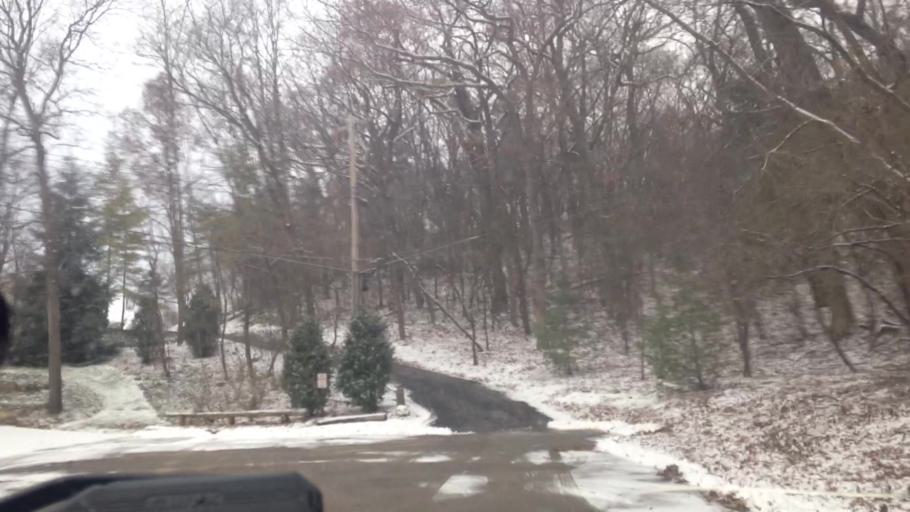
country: US
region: Wisconsin
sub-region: Waukesha County
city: Delafield
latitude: 43.0655
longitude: -88.3798
